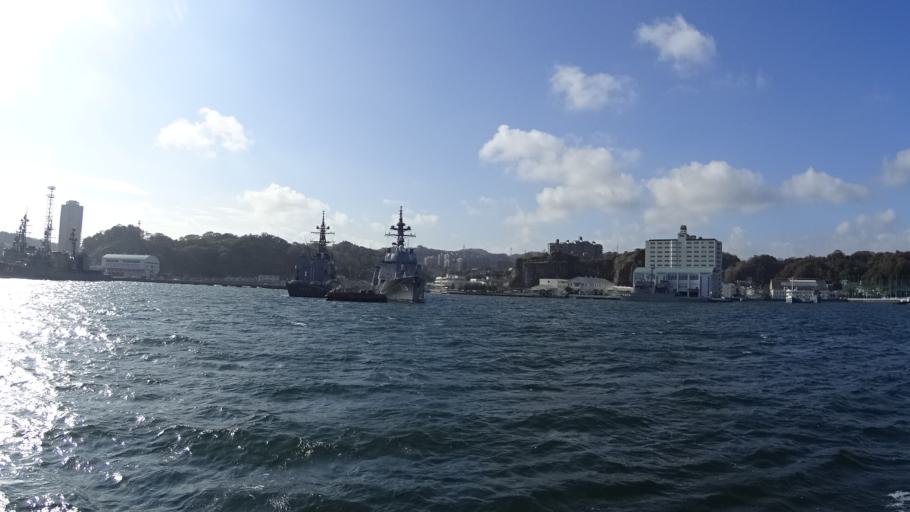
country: JP
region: Kanagawa
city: Yokosuka
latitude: 35.2926
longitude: 139.6525
